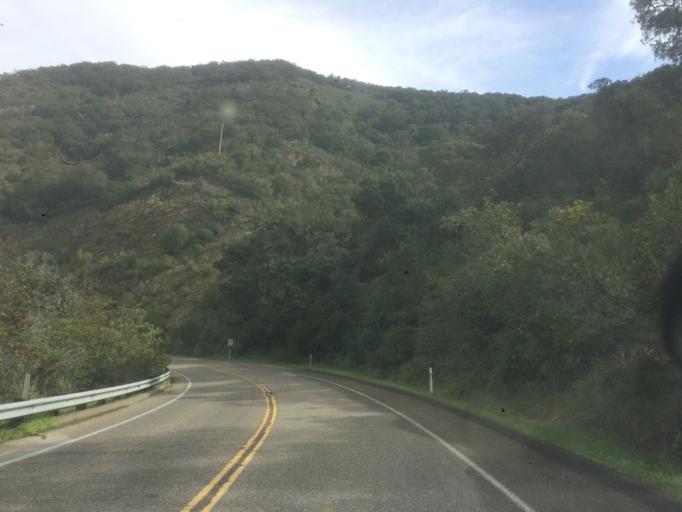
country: US
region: California
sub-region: San Luis Obispo County
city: Arroyo Grande
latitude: 35.1866
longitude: -120.4759
